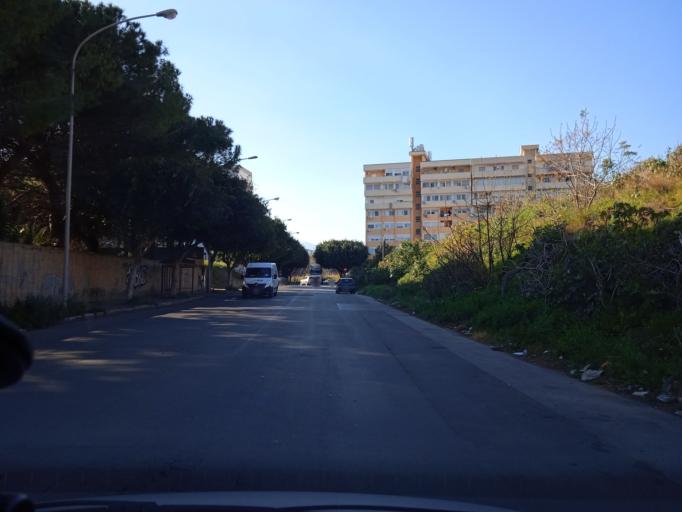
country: IT
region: Sicily
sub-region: Palermo
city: Ciaculli
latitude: 38.1073
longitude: 13.3787
